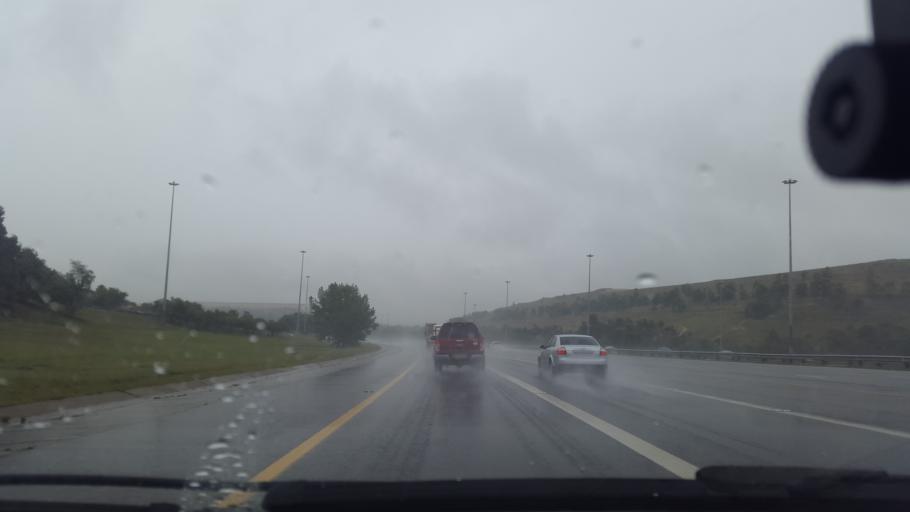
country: ZA
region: Gauteng
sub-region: City of Johannesburg Metropolitan Municipality
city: Johannesburg
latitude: -26.2495
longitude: 27.9639
